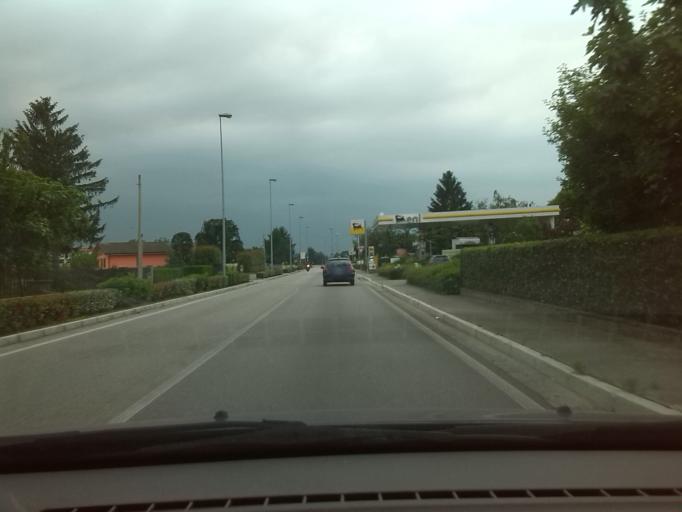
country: IT
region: Friuli Venezia Giulia
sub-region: Provincia di Udine
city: Santo Stefano
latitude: 46.2039
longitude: 13.1214
